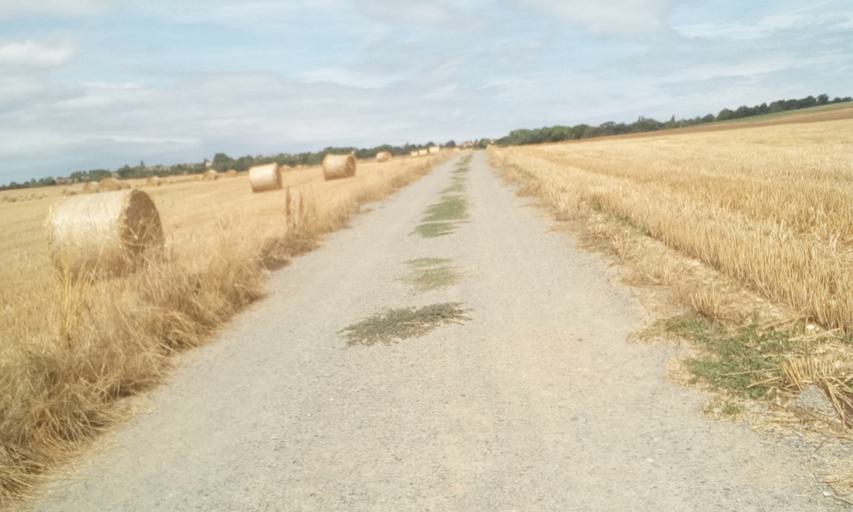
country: FR
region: Lower Normandy
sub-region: Departement du Calvados
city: Herouvillette
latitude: 49.2302
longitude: -0.2344
